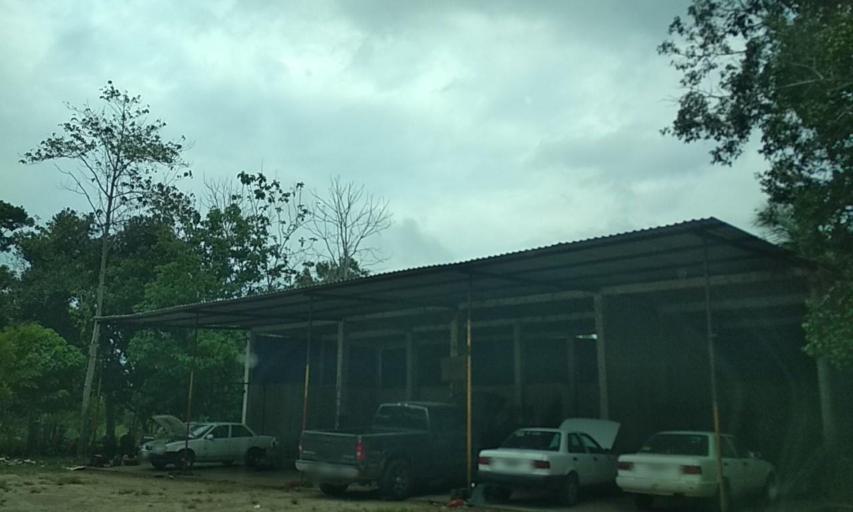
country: MX
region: Veracruz
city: Las Choapas
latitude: 17.8712
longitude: -94.1014
